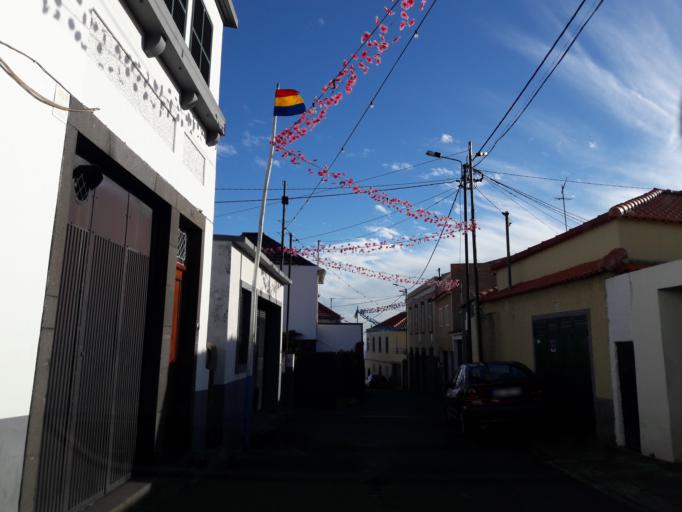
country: PT
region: Madeira
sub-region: Funchal
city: Nossa Senhora do Monte
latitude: 32.6642
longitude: -16.9228
